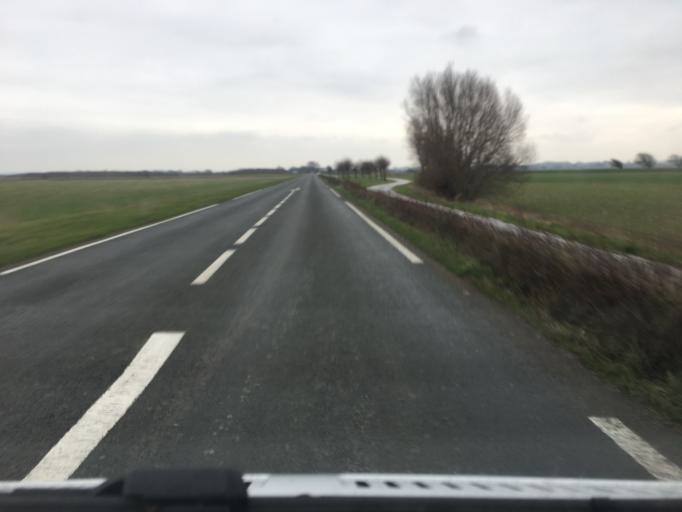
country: FR
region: Picardie
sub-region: Departement de la Somme
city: Pende
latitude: 50.1976
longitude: 1.5560
